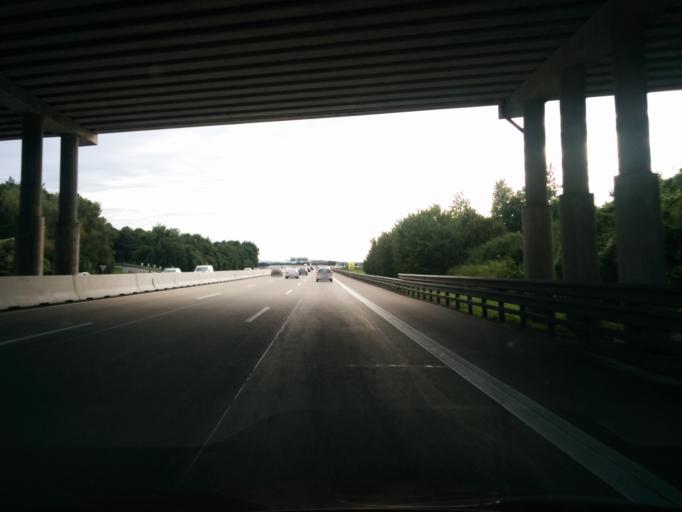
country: AT
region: Lower Austria
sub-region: Politischer Bezirk Sankt Polten
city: Pyhra
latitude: 48.1800
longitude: 15.6626
